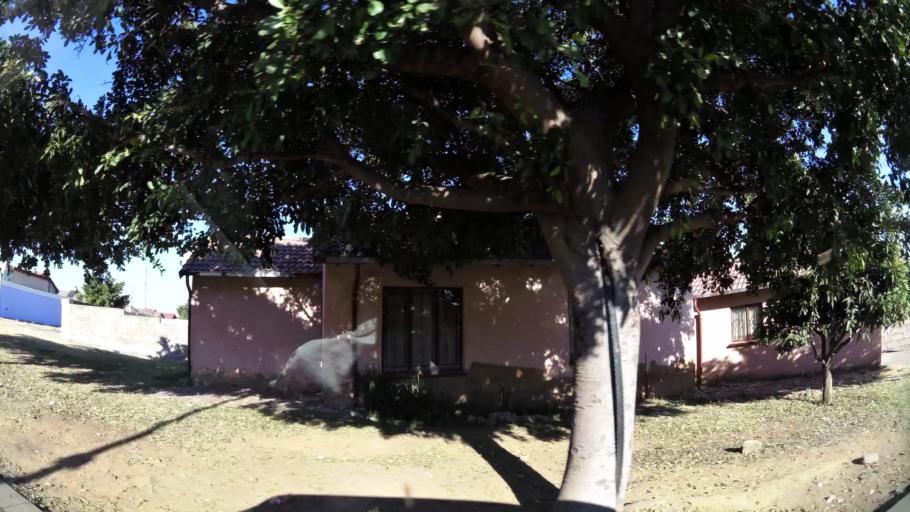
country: ZA
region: Gauteng
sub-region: City of Johannesburg Metropolitan Municipality
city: Modderfontein
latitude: -26.0418
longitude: 28.1601
